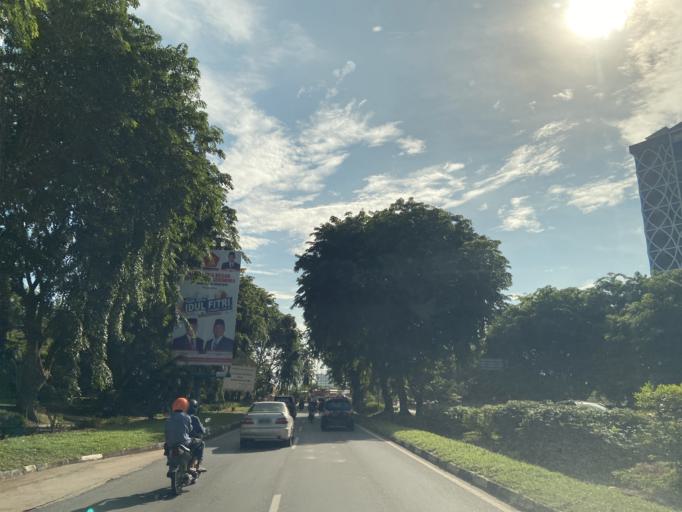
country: SG
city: Singapore
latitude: 1.1183
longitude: 104.0463
